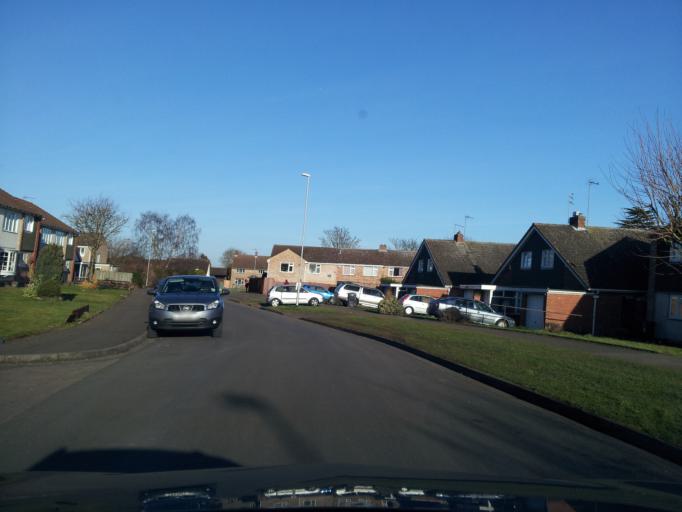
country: GB
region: England
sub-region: Northamptonshire
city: Northampton
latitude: 52.2490
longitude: -0.9518
